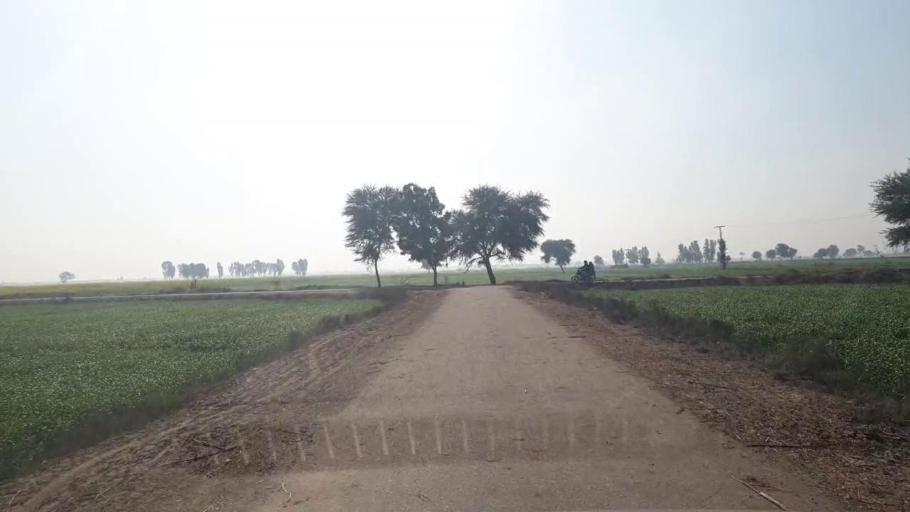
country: PK
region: Sindh
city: Shahdadpur
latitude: 25.9630
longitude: 68.5877
